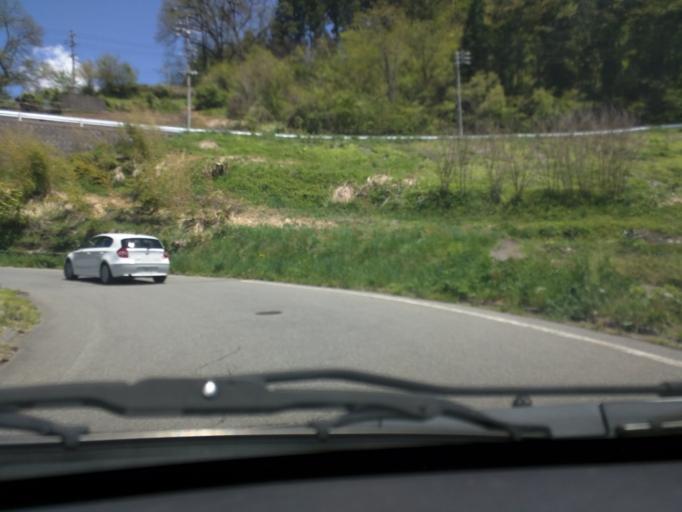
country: JP
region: Nagano
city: Nagano-shi
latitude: 36.6755
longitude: 138.1094
